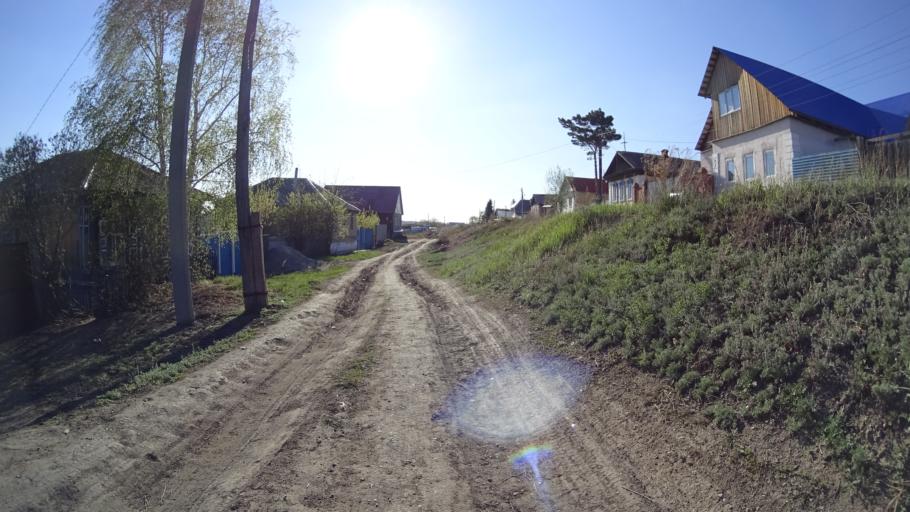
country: RU
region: Chelyabinsk
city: Troitsk
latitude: 54.0993
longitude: 61.5445
